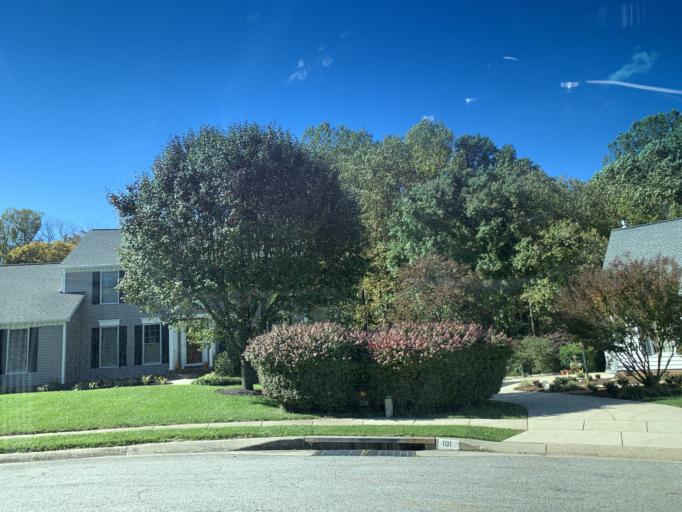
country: US
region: Maryland
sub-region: Harford County
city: Bel Air South
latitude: 39.5127
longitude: -76.3220
